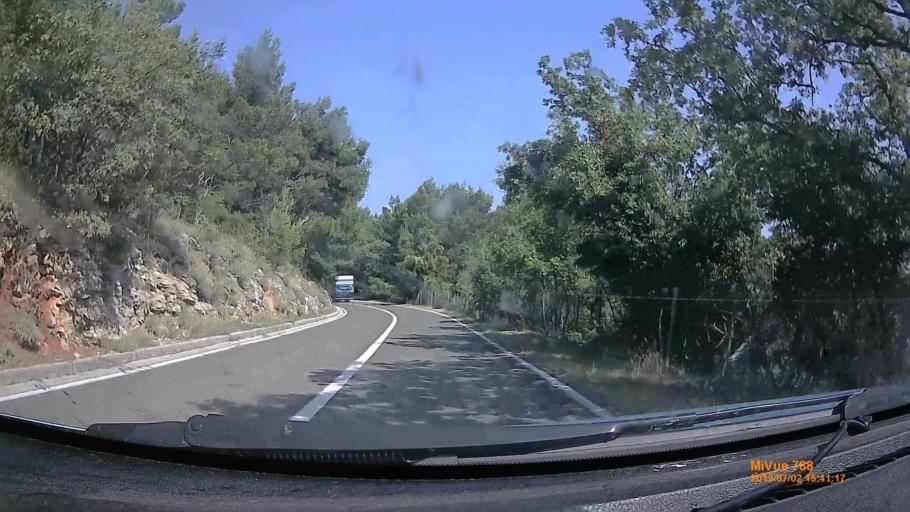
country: HR
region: Primorsko-Goranska
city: Cres
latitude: 44.9607
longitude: 14.4403
